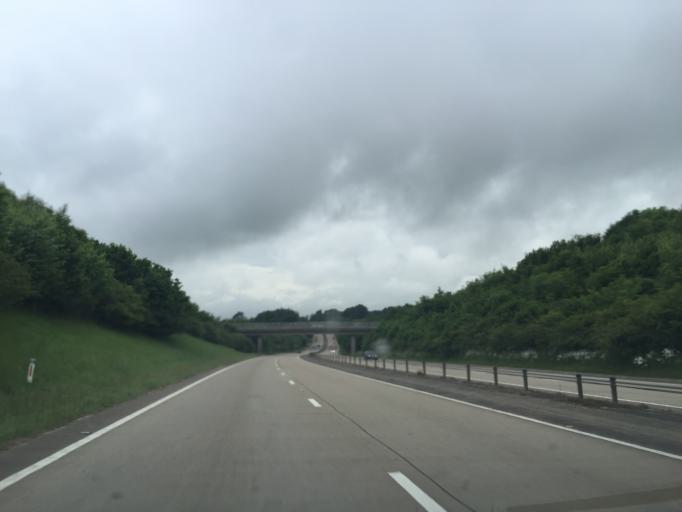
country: GB
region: England
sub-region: Dorset
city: Bovington Camp
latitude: 50.7528
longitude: -2.3164
